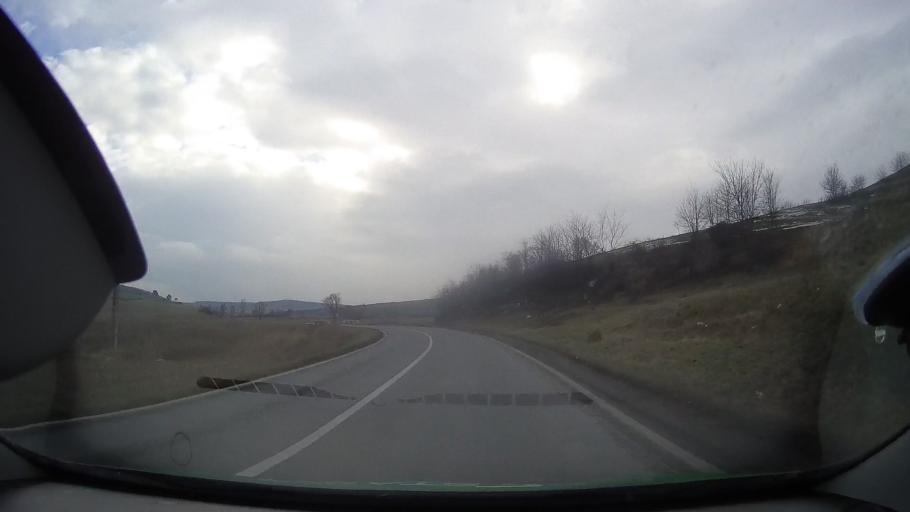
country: RO
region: Mures
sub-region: Comuna Cucerdea
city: Cucerdea
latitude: 46.3845
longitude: 24.2546
